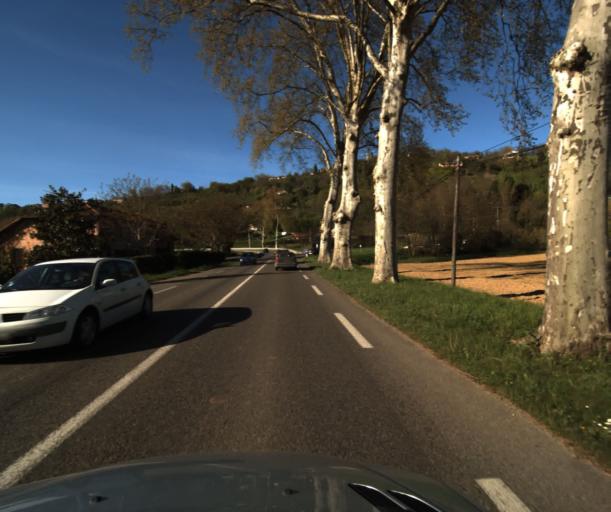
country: FR
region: Midi-Pyrenees
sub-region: Departement du Tarn-et-Garonne
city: Lafrancaise
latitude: 44.1181
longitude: 1.2485
